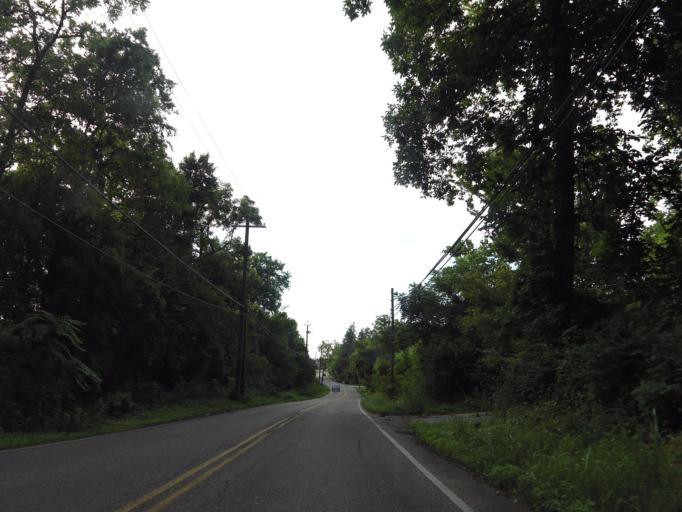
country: US
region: Tennessee
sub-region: Knox County
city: Farragut
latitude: 35.9106
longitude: -84.0778
